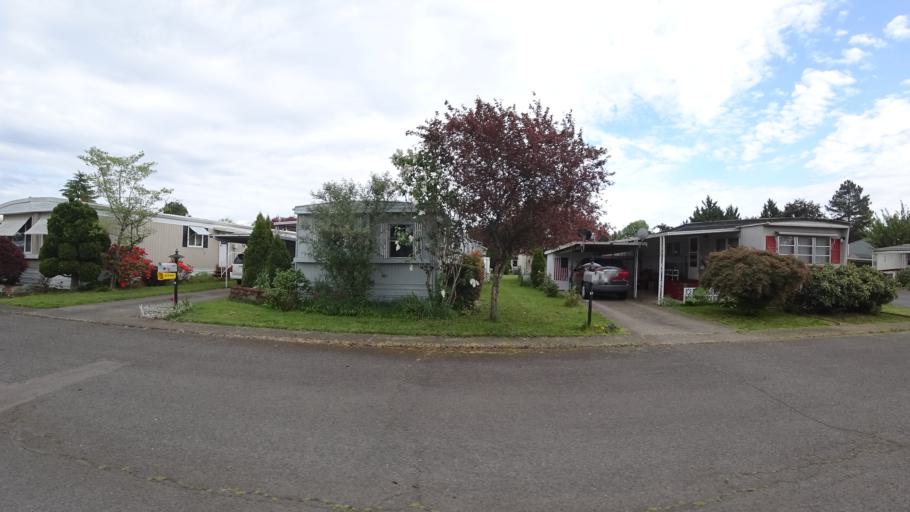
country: US
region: Oregon
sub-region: Washington County
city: Hillsboro
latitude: 45.5015
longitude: -122.9552
